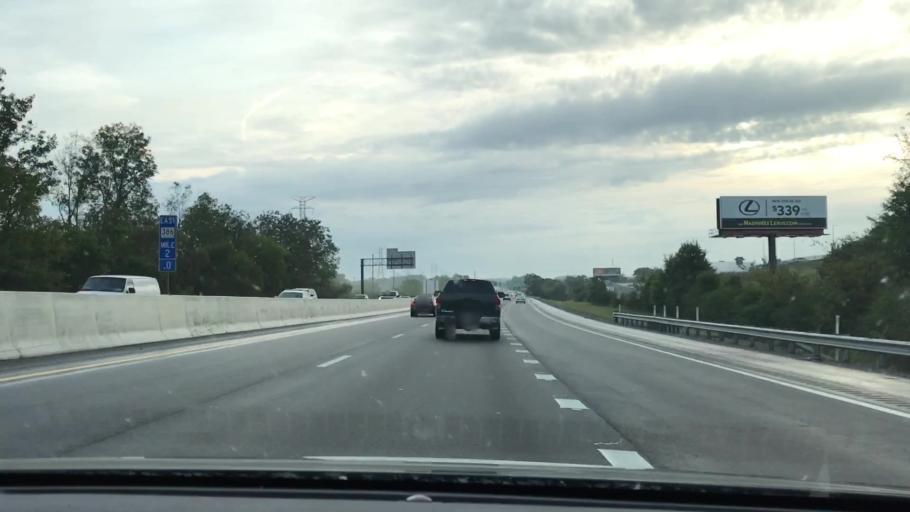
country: US
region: Tennessee
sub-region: Davidson County
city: Goodlettsville
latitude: 36.3120
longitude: -86.6794
